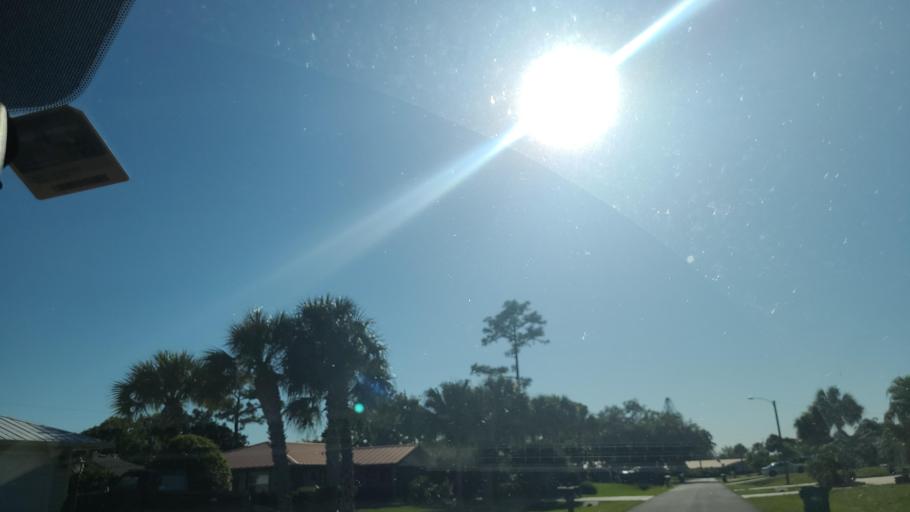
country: US
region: Florida
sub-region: Indian River County
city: Sebastian
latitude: 27.8008
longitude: -80.4913
